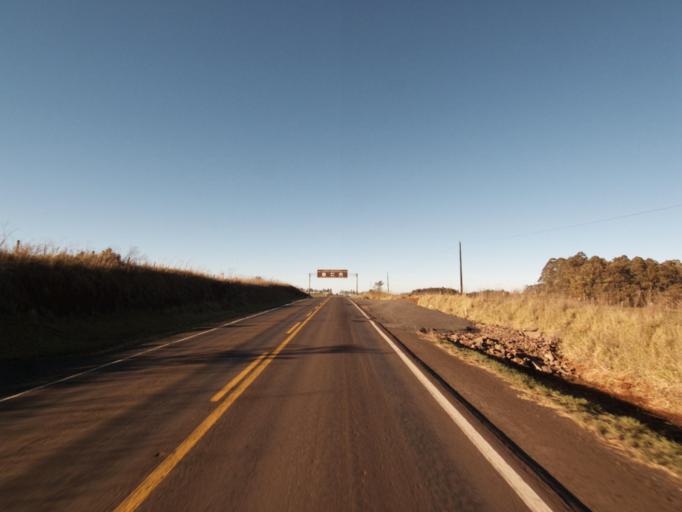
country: AR
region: Misiones
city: Bernardo de Irigoyen
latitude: -26.2980
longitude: -53.5537
